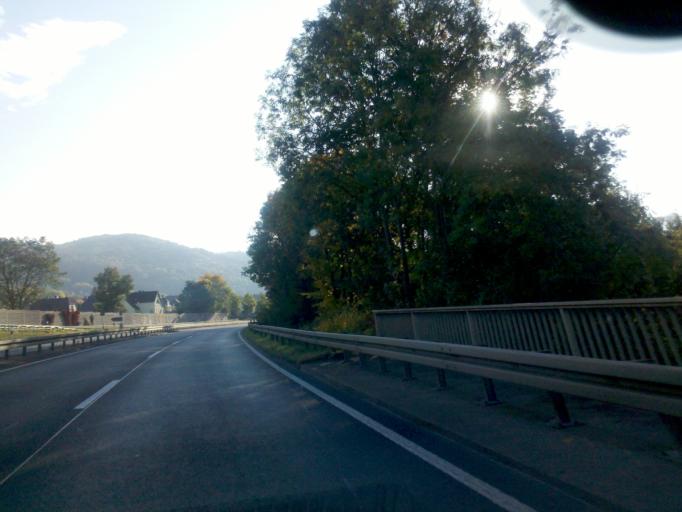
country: DE
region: Hesse
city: Dillenburg
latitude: 50.7426
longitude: 8.2757
